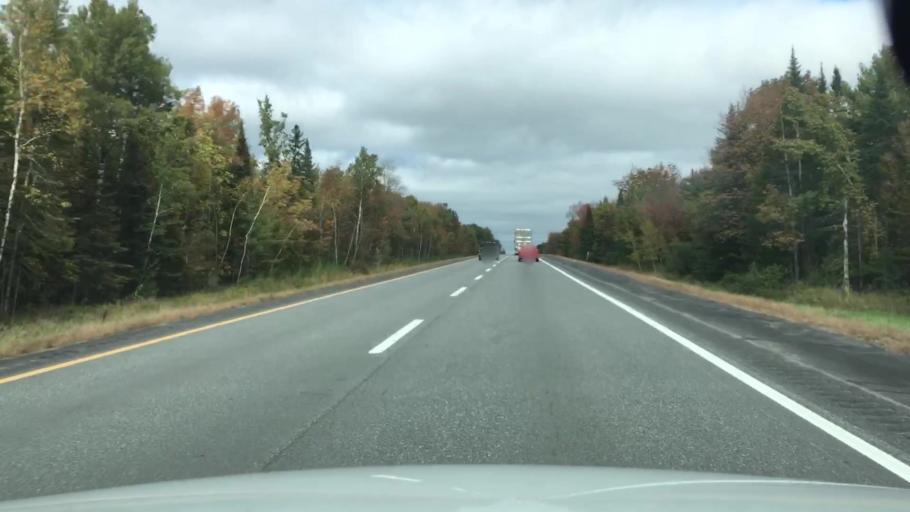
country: US
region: Maine
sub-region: Somerset County
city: Palmyra
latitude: 44.8203
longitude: -69.3311
